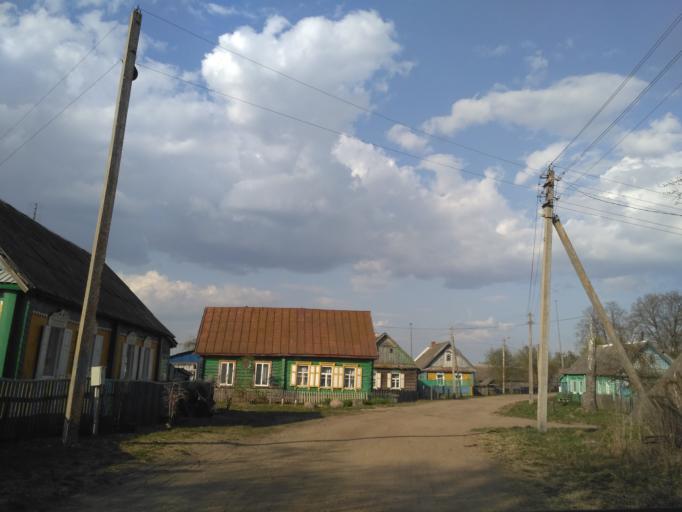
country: BY
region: Minsk
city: Khalopyenichy
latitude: 54.5066
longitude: 28.8518
